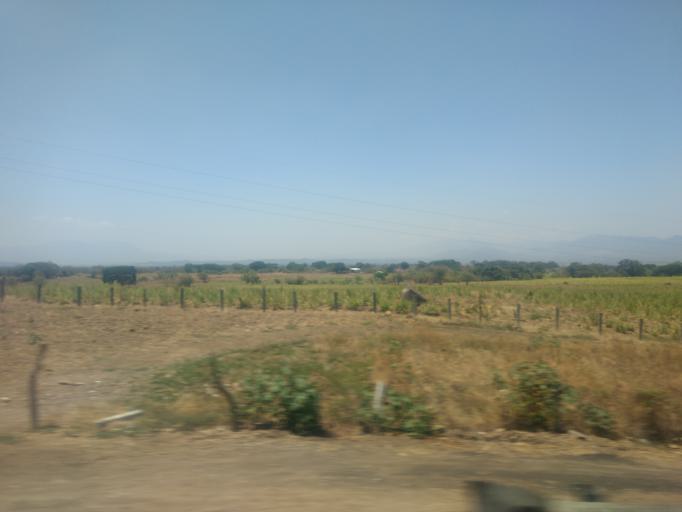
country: MX
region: Colima
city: Cuauhtemoc
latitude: 19.3040
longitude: -103.6228
